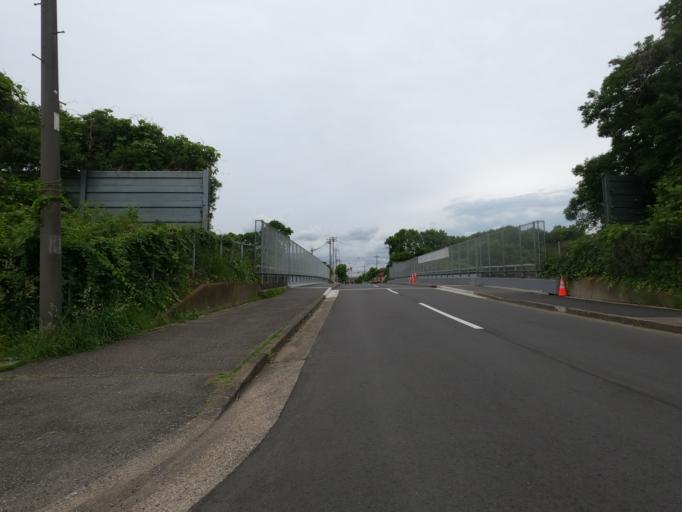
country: JP
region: Ibaraki
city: Moriya
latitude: 35.9641
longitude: 139.9787
